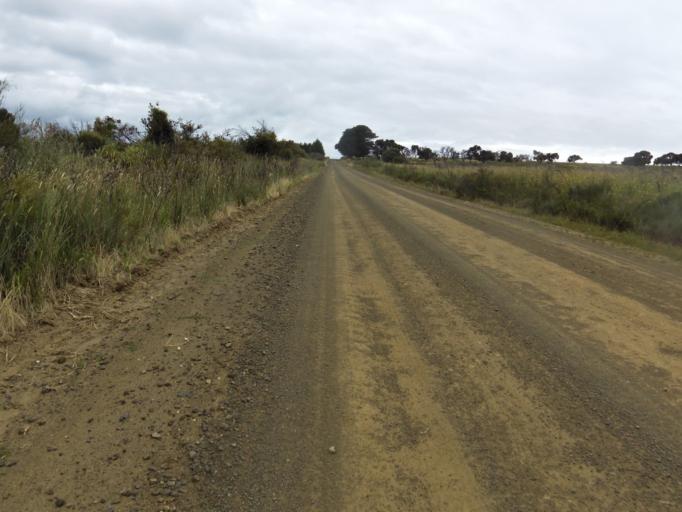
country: AU
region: Victoria
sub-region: Bass Coast
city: Cowes
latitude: -38.3805
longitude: 145.3556
